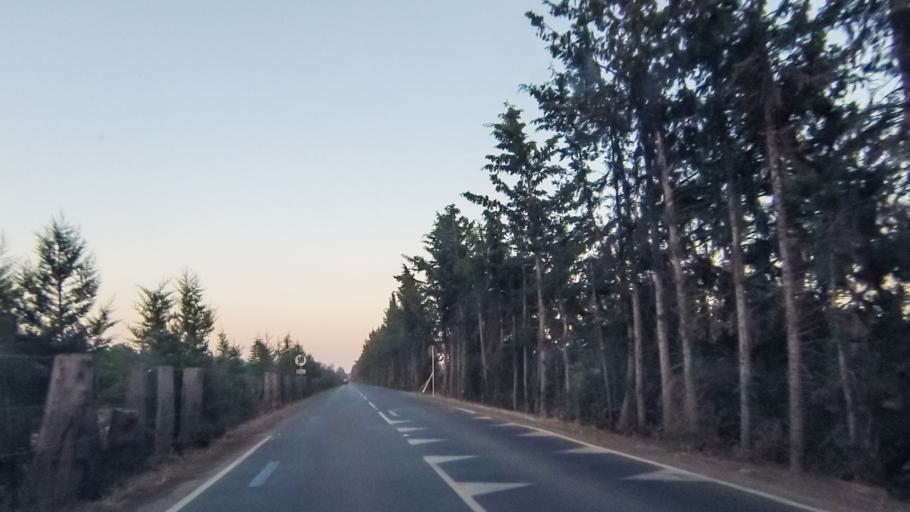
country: CY
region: Larnaka
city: Kolossi
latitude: 34.6369
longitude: 32.9482
